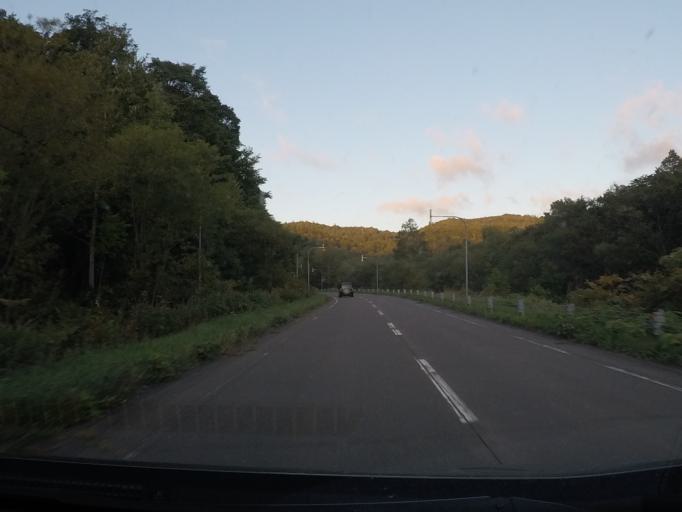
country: JP
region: Hokkaido
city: Nayoro
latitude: 44.3604
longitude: 142.2911
